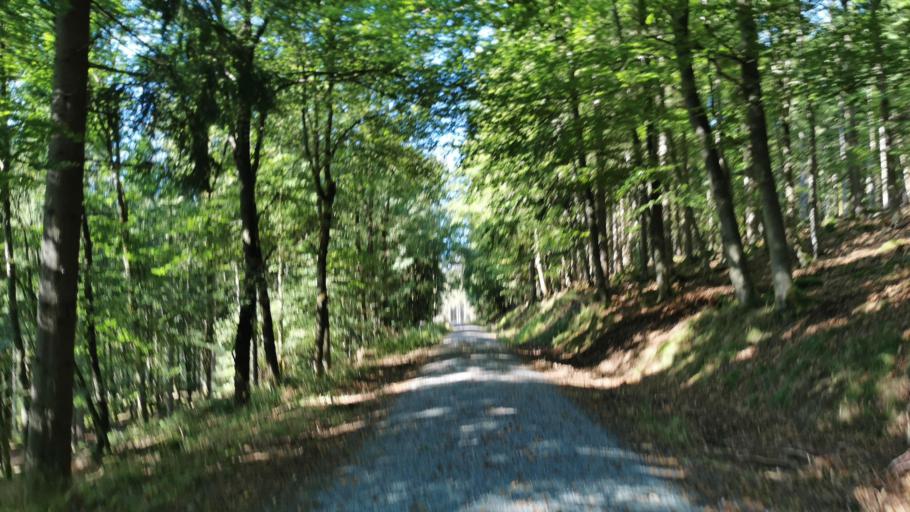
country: DE
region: Bavaria
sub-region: Upper Franconia
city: Ludwigsstadt
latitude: 50.4448
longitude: 11.3488
